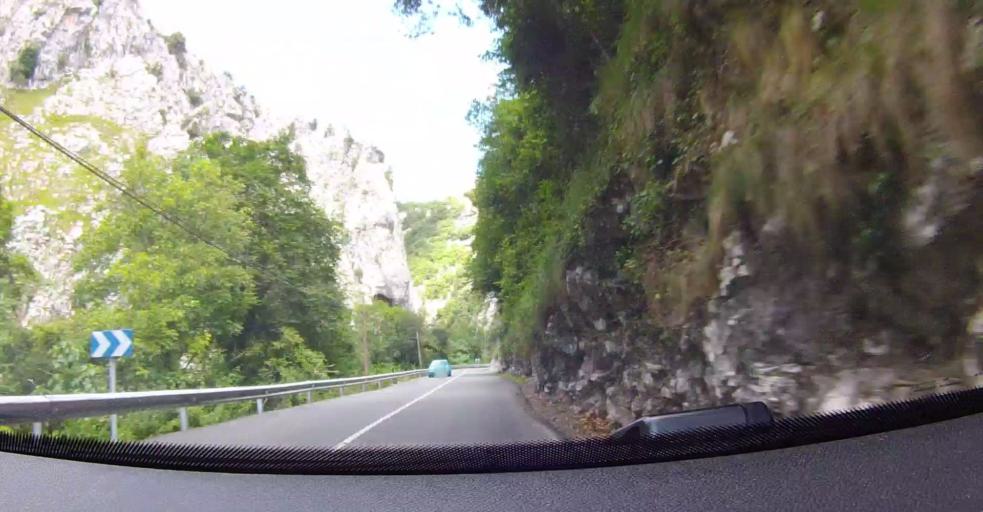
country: ES
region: Cantabria
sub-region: Provincia de Cantabria
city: Tresviso
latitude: 43.3018
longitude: -4.6063
